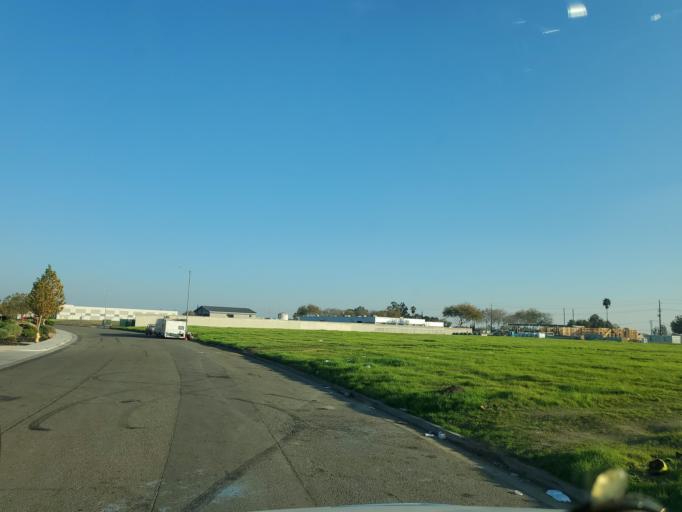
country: US
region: California
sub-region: San Joaquin County
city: Kennedy
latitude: 37.9075
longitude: -121.2207
